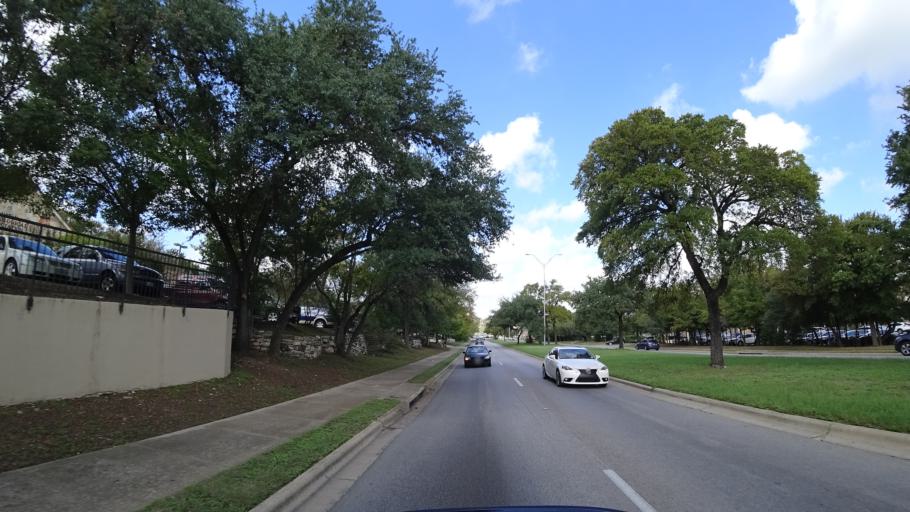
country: US
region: Texas
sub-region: Travis County
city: Shady Hollow
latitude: 30.2061
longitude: -97.8132
